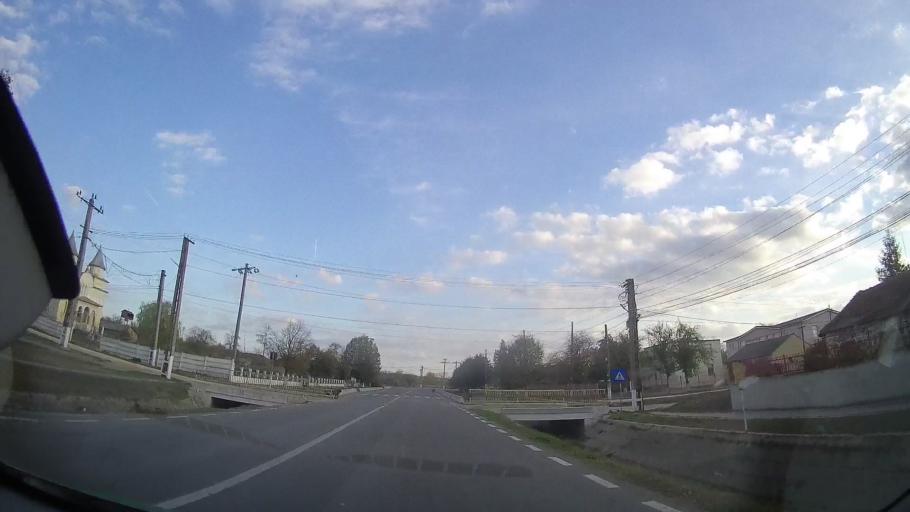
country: RO
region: Constanta
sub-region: Comuna Independenta
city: Independenta
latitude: 43.9498
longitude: 28.0849
